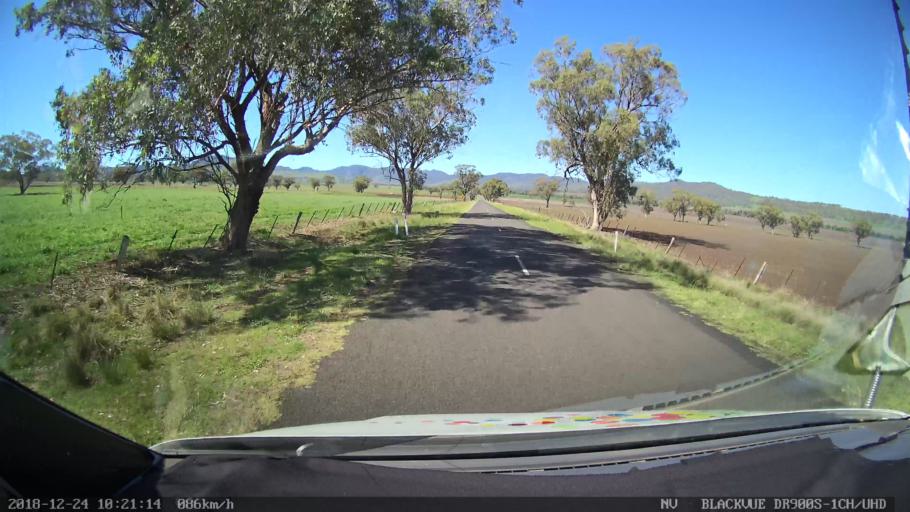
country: AU
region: New South Wales
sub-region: Liverpool Plains
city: Quirindi
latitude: -31.7497
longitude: 150.5522
